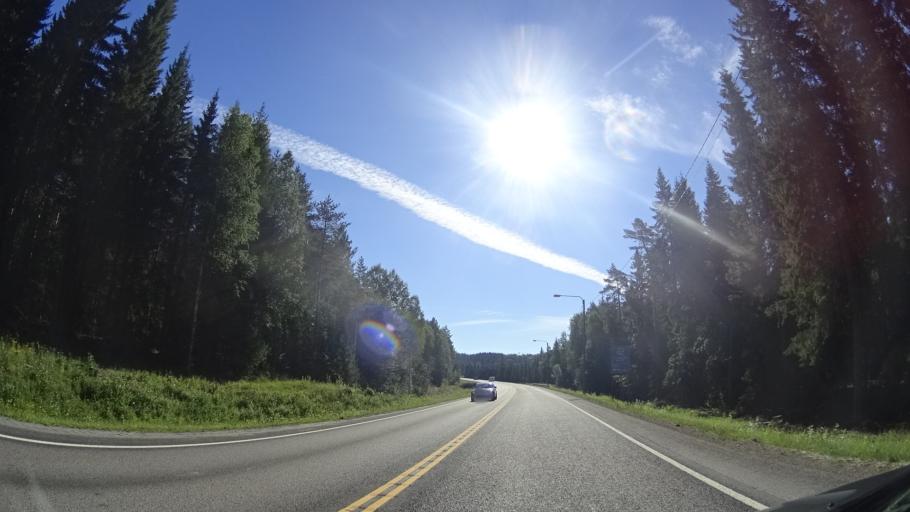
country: FI
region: Central Finland
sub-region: Jyvaeskylae
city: Petaejaevesi
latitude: 62.2706
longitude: 25.3302
